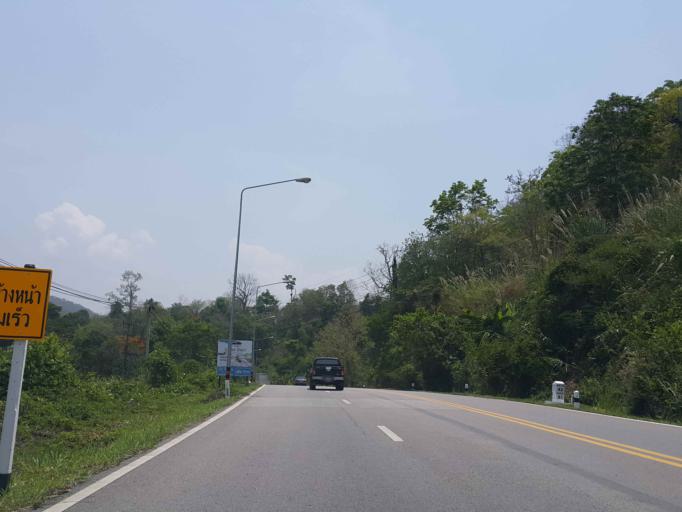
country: TH
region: Chiang Mai
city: Mae On
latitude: 18.9734
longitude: 99.2535
